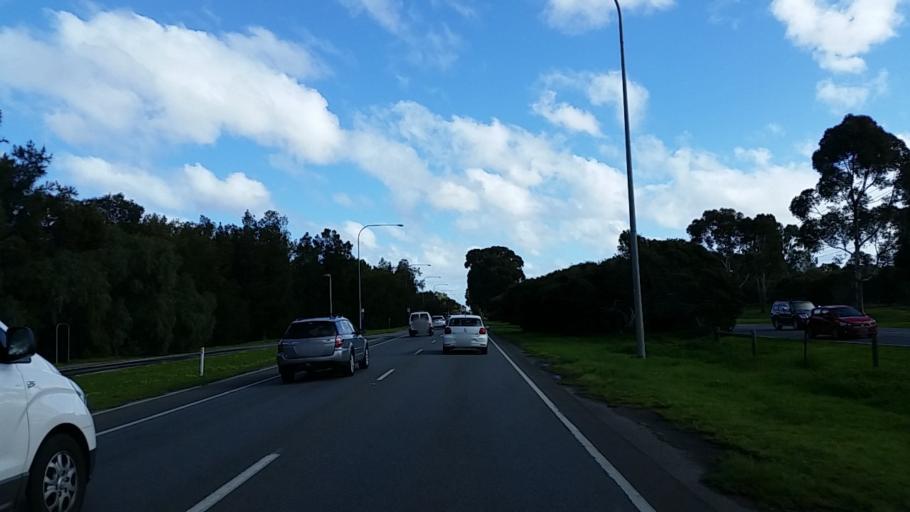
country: AU
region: South Australia
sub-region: Salisbury
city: Ingle Farm
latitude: -34.8169
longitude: 138.6246
